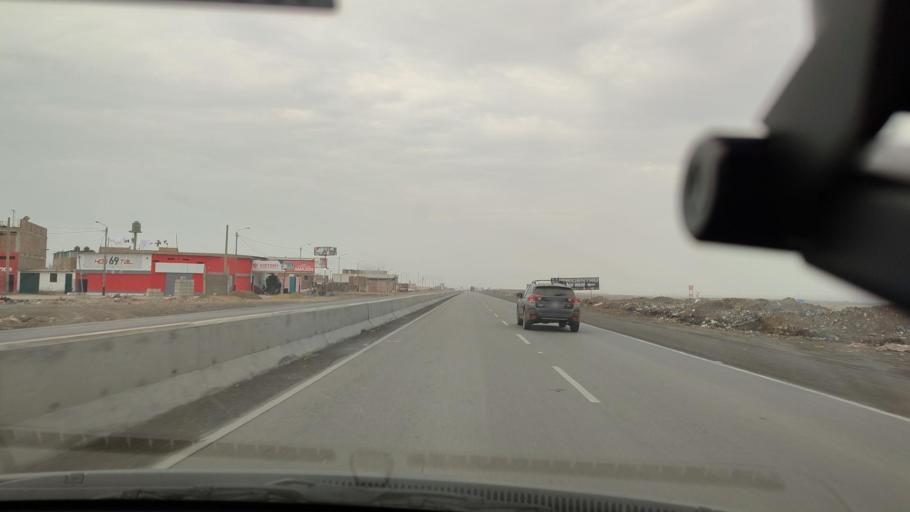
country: PE
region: La Libertad
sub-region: Provincia de Trujillo
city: La Esperanza
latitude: -8.0192
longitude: -79.0742
